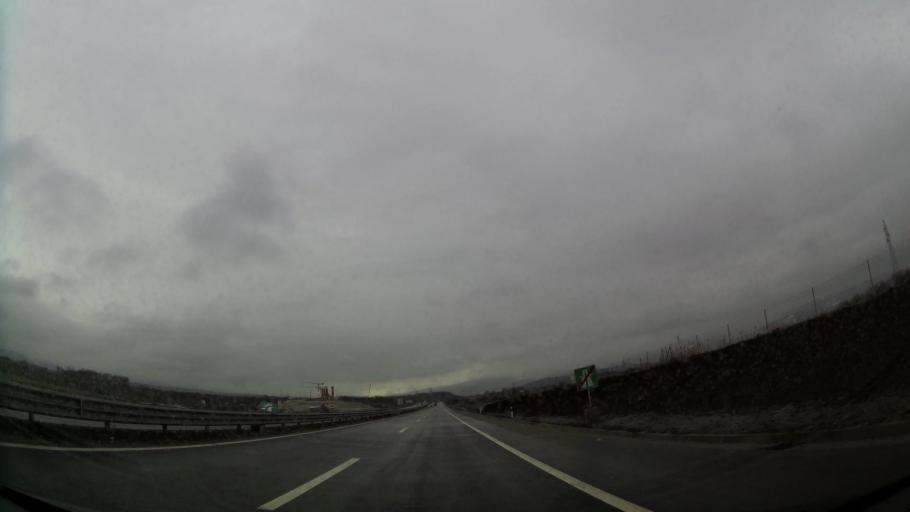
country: XK
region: Ferizaj
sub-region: Komuna e Kacanikut
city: Kacanik
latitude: 42.2839
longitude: 21.2088
